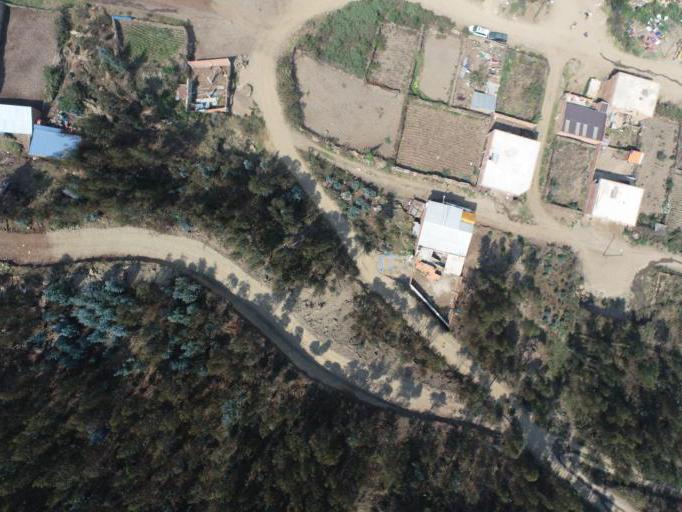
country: BO
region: La Paz
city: Quime
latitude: -16.9854
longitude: -67.2133
